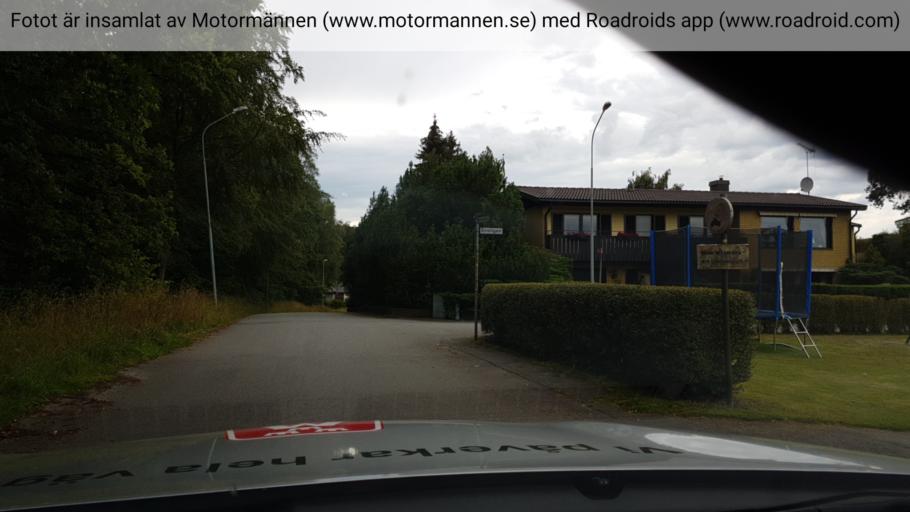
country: SE
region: Skane
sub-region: Hassleholms Kommun
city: Hassleholm
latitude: 56.1538
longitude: 13.7462
